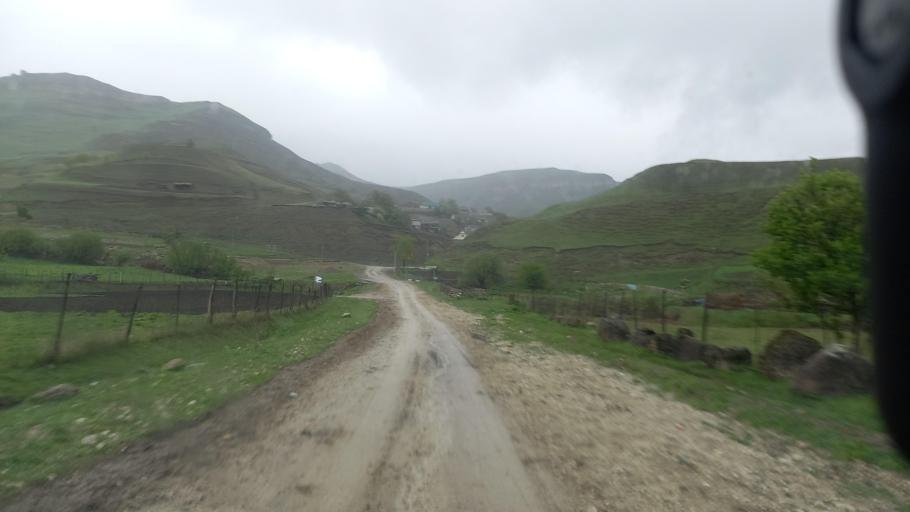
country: RU
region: Kabardino-Balkariya
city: Gundelen
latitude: 43.5983
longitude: 43.1441
